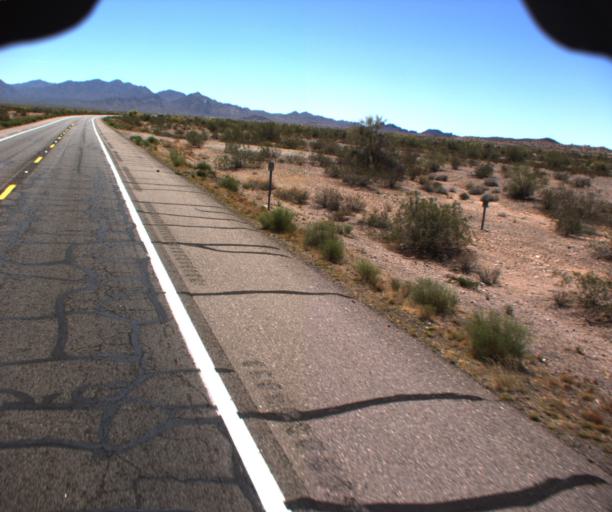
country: US
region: Arizona
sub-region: Mohave County
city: Desert Hills
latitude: 34.7113
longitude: -114.3065
